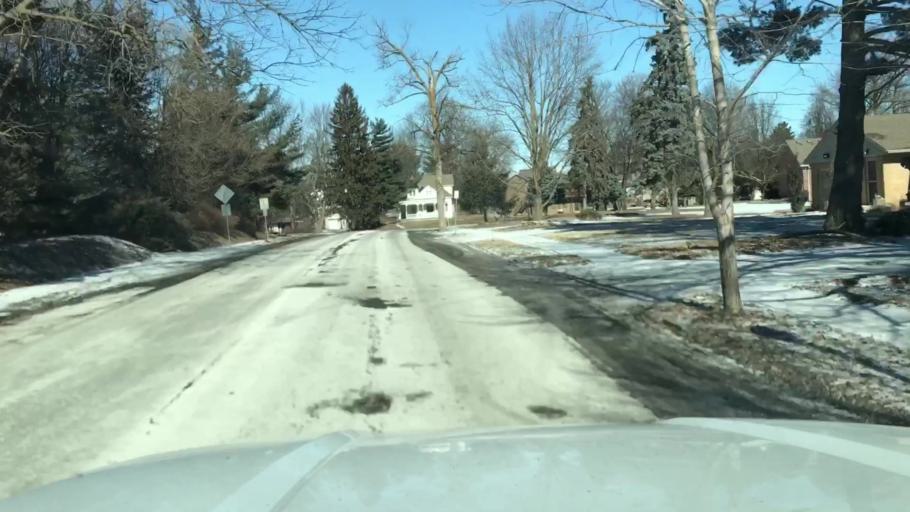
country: US
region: Missouri
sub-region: Andrew County
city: Country Club Village
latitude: 39.7971
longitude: -94.8194
